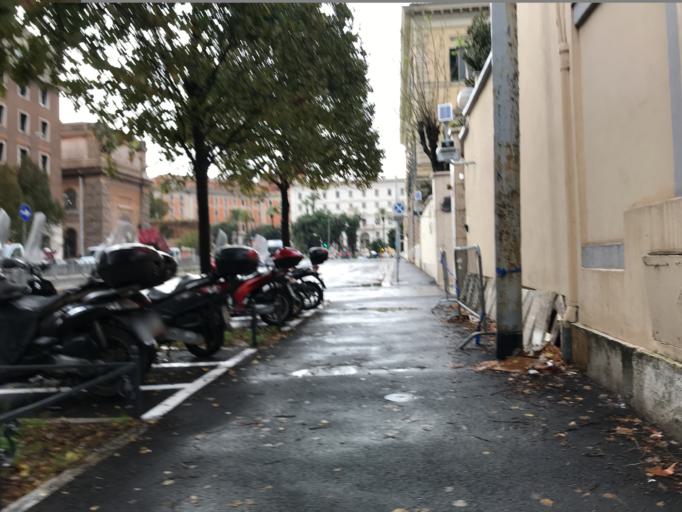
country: IT
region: Latium
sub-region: Citta metropolitana di Roma Capitale
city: Rome
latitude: 41.9071
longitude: 12.5053
